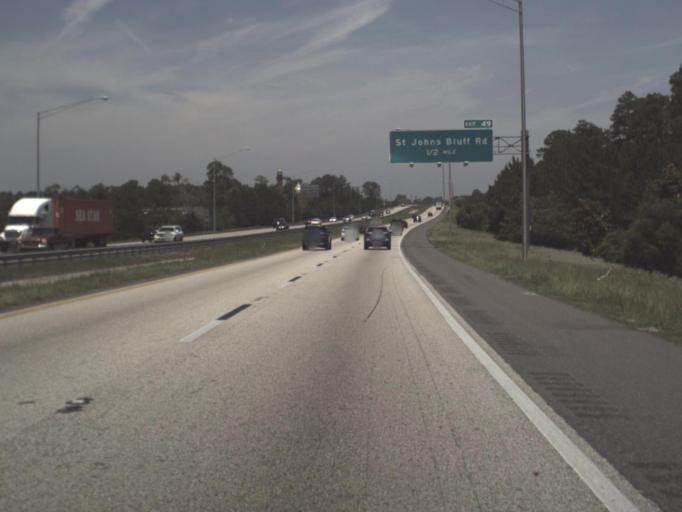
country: US
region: Florida
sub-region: Duval County
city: Neptune Beach
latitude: 30.3028
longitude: -81.5234
